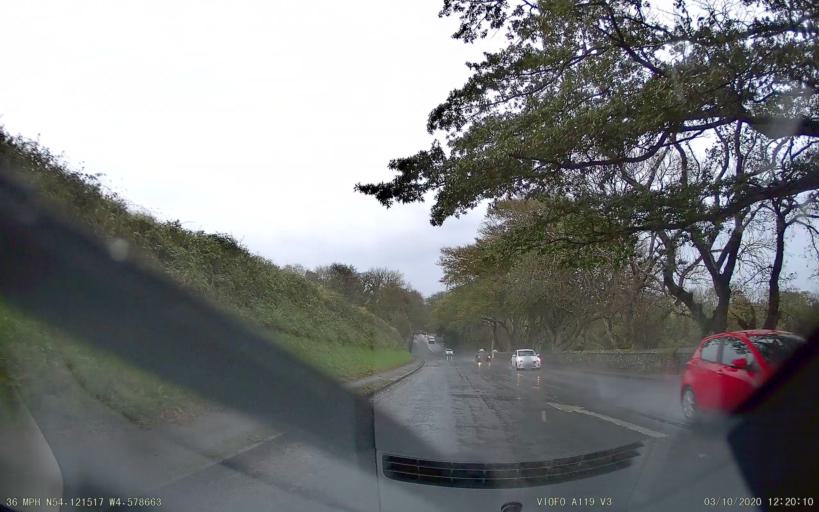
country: IM
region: Castletown
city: Castletown
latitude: 54.1215
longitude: -4.5787
